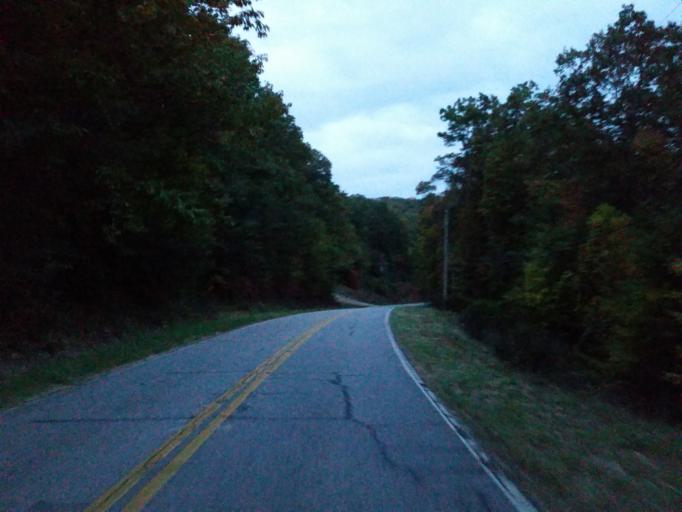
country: US
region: Georgia
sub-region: Lumpkin County
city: Dahlonega
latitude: 34.6347
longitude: -83.9559
